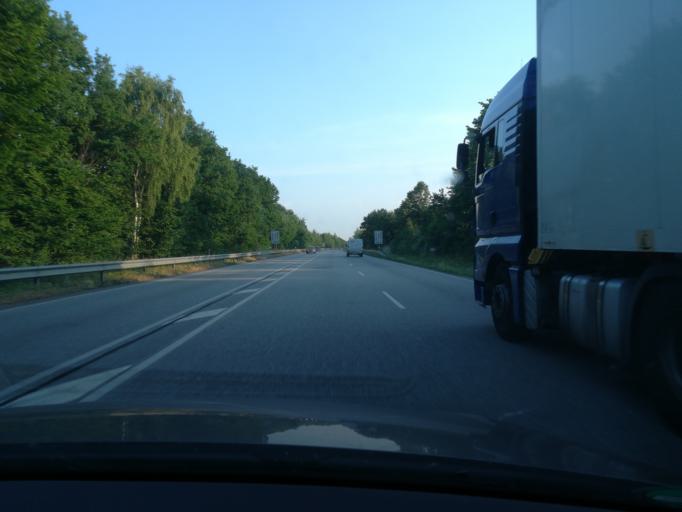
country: DE
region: Schleswig-Holstein
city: Kasseburg
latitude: 53.5689
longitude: 10.4036
